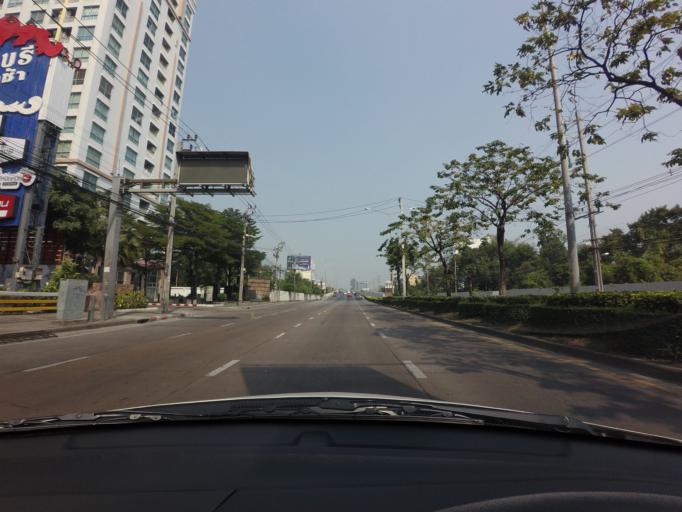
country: TH
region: Bangkok
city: Bangkok Yai
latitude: 13.7179
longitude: 100.4777
